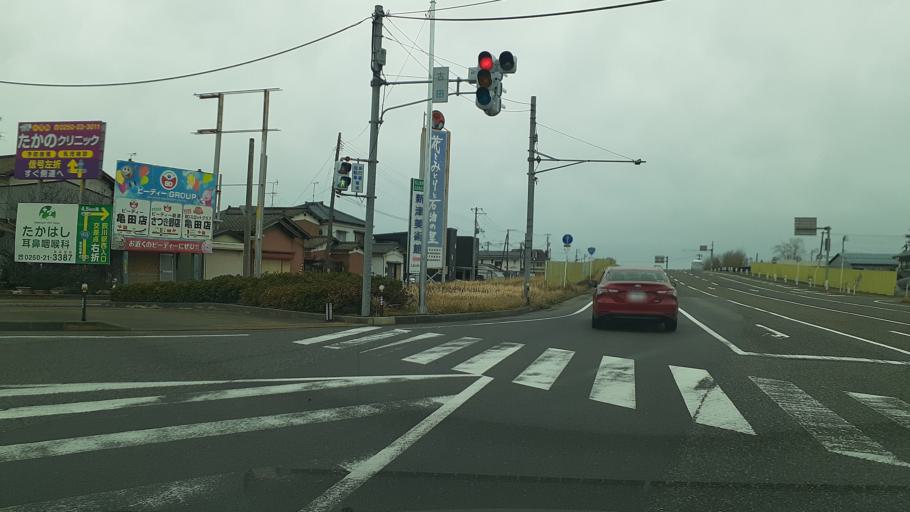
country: JP
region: Niigata
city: Niitsu-honcho
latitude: 37.7945
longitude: 139.1089
